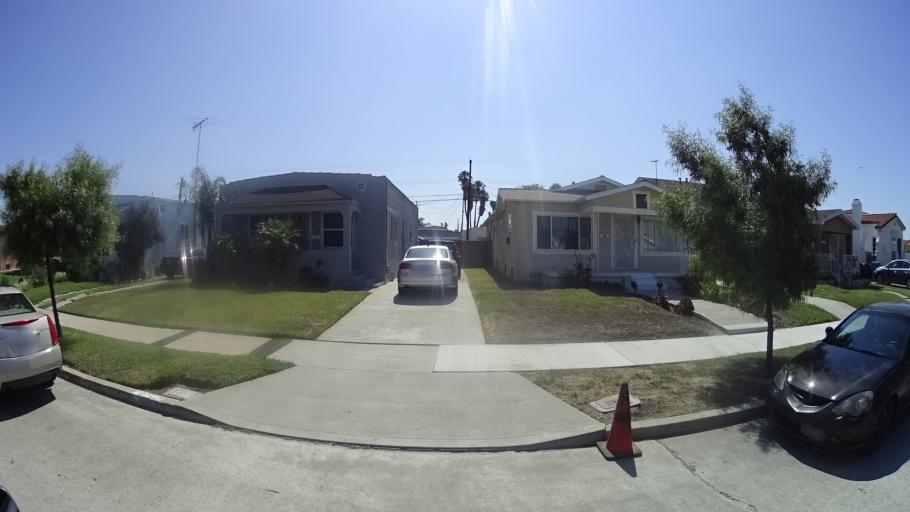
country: US
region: California
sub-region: Los Angeles County
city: View Park-Windsor Hills
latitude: 33.9822
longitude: -118.3168
